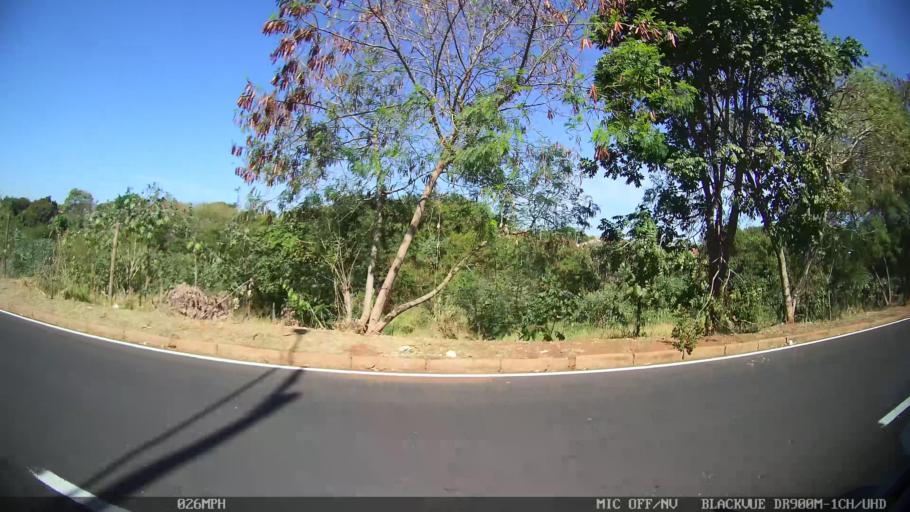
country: BR
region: Sao Paulo
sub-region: Sao Jose Do Rio Preto
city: Sao Jose do Rio Preto
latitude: -20.7732
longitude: -49.4086
